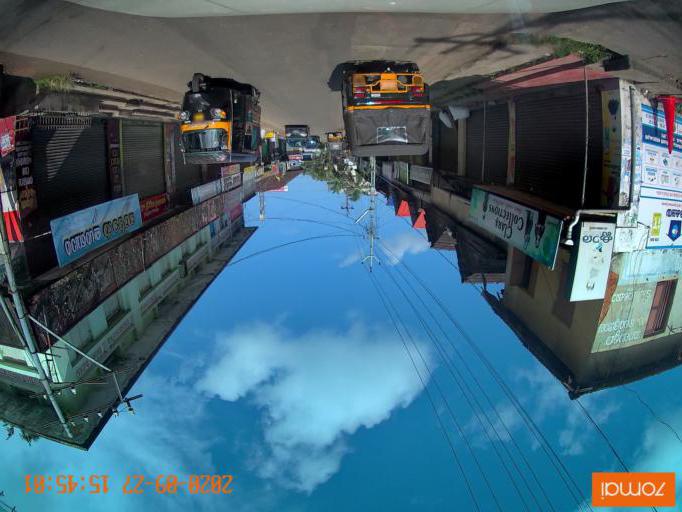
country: IN
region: Kerala
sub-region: Thrissur District
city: Thanniyam
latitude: 10.4771
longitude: 76.1143
